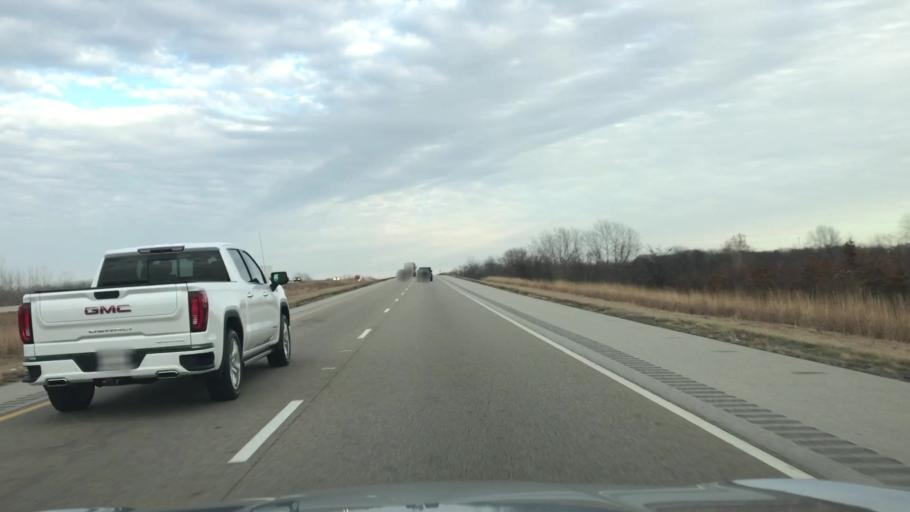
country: US
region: Illinois
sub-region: Logan County
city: Lincoln
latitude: 40.1815
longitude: -89.3833
